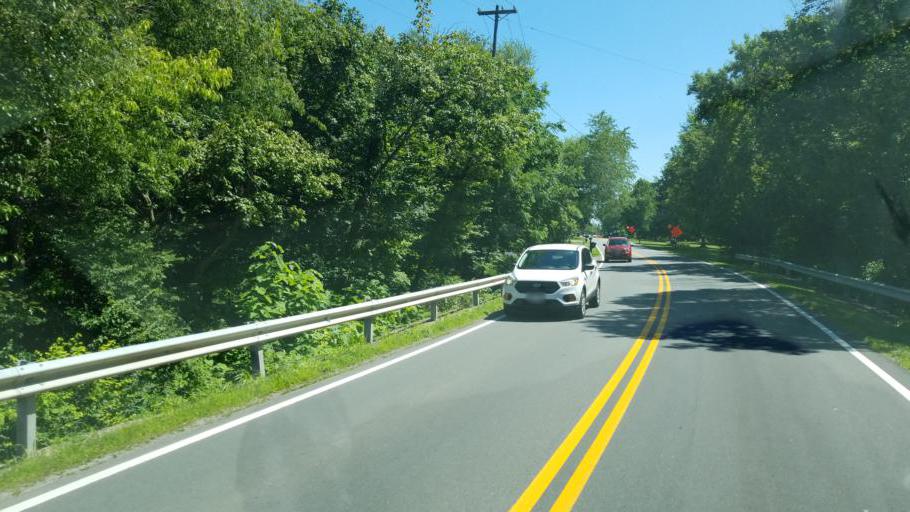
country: US
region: Ohio
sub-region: Franklin County
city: Westerville
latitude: 40.1480
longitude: -82.8829
